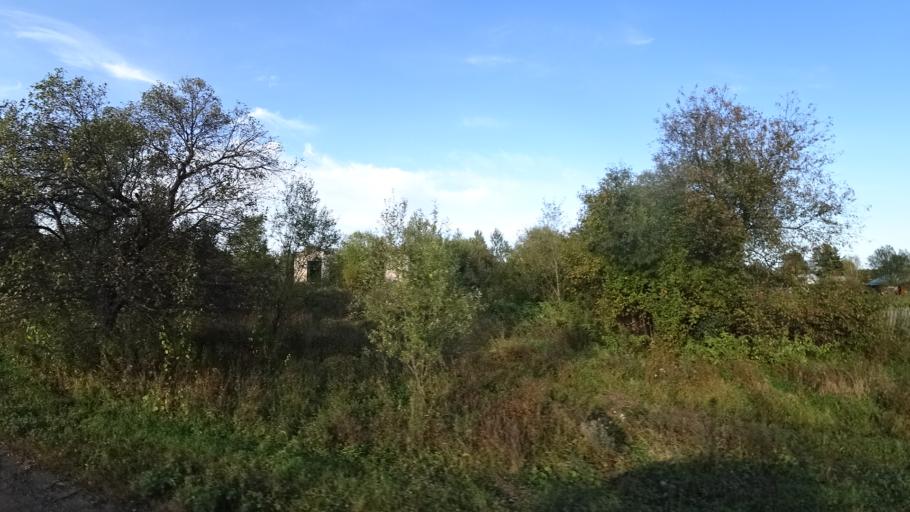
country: RU
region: Amur
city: Arkhara
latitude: 49.3615
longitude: 130.1249
